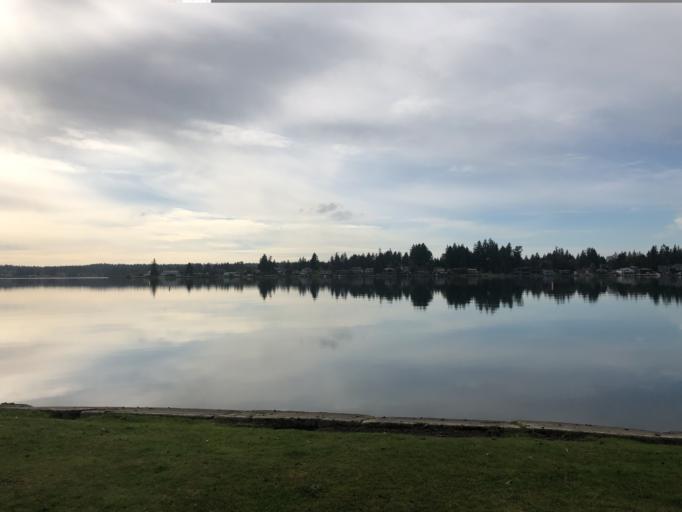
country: US
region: Washington
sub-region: Pierce County
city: Bonney Lake
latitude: 47.2401
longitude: -122.1685
